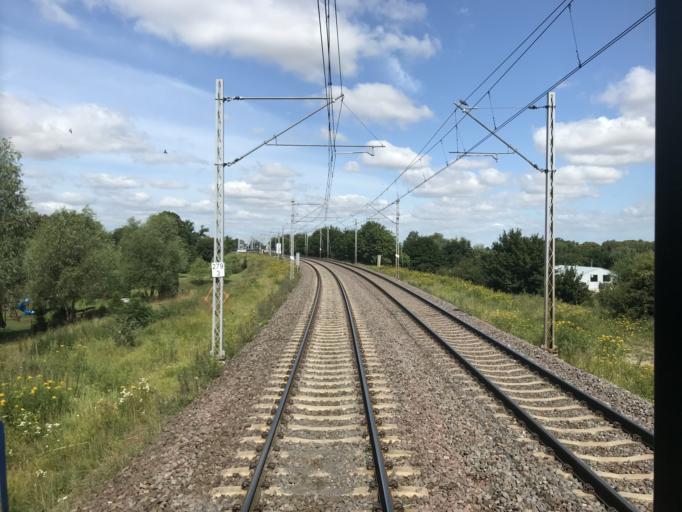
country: PL
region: Pomeranian Voivodeship
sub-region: Powiat malborski
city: Malbork
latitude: 54.0452
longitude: 19.0287
